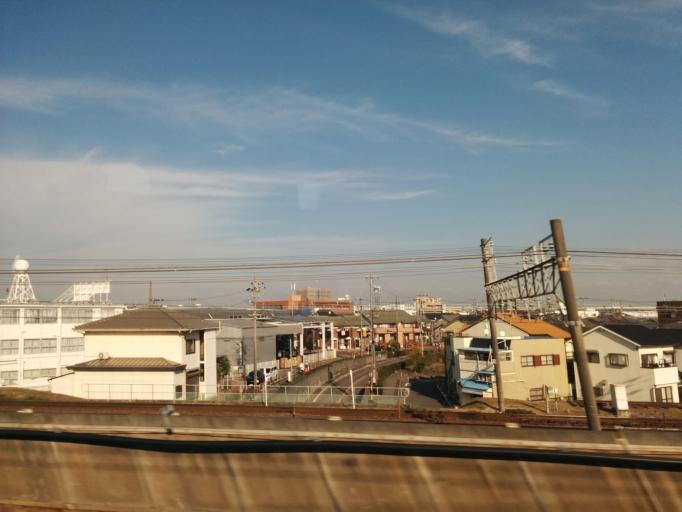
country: JP
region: Aichi
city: Inazawa
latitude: 35.2147
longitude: 136.8437
